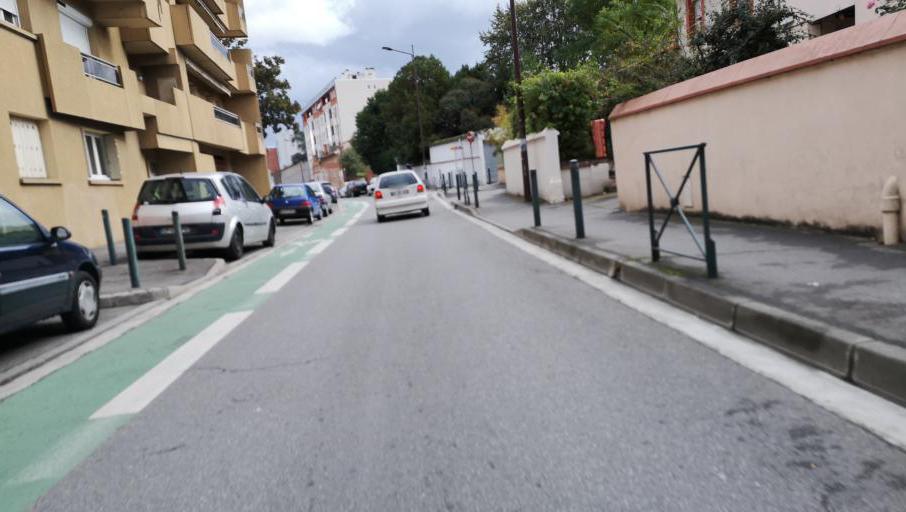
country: FR
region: Midi-Pyrenees
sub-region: Departement de la Haute-Garonne
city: Toulouse
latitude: 43.6006
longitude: 1.4206
